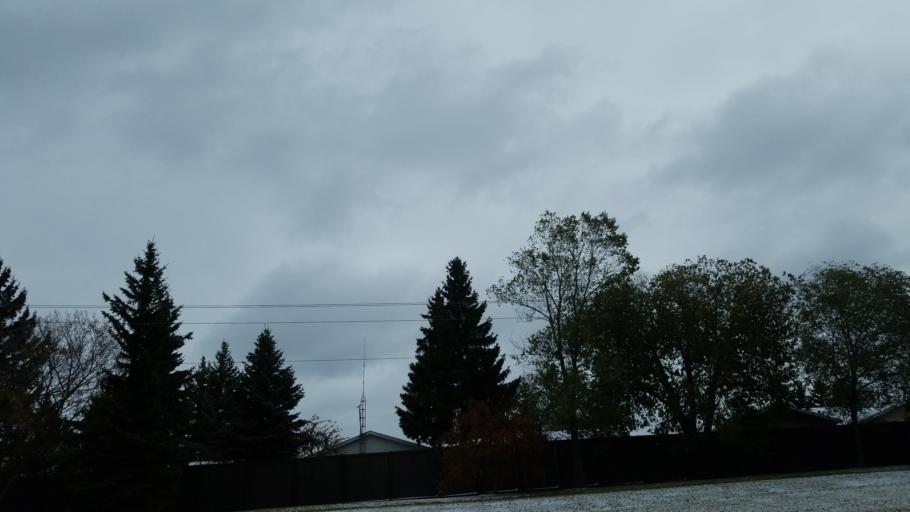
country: CA
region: Alberta
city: Sherwood Park
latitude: 53.5353
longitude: -113.2958
